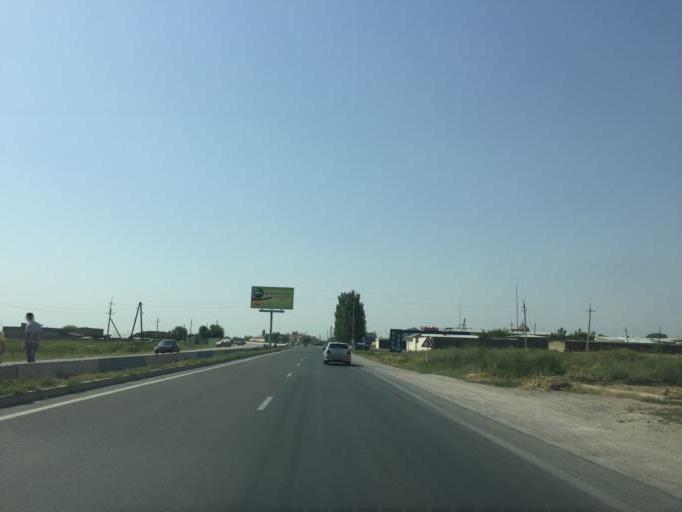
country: AM
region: Ararat
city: Artashat
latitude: 39.9534
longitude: 44.5387
